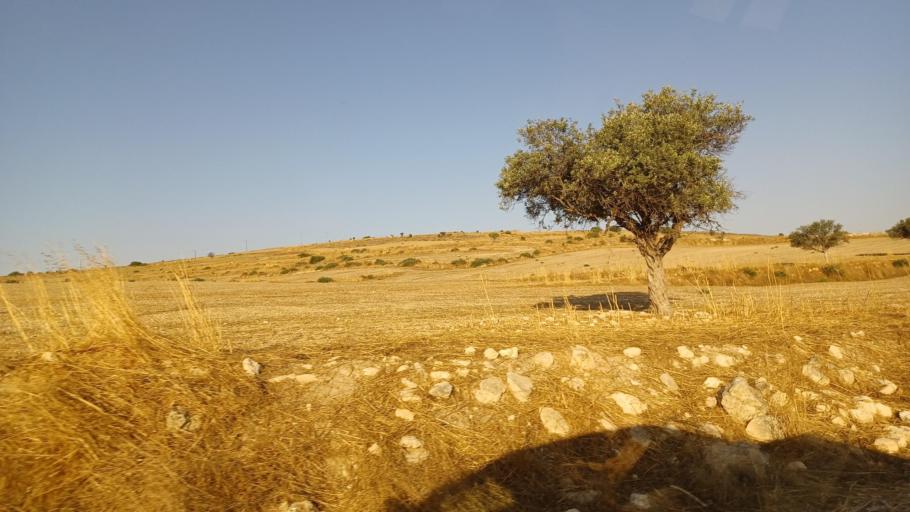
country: CY
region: Larnaka
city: Athienou
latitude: 35.0475
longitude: 33.5137
